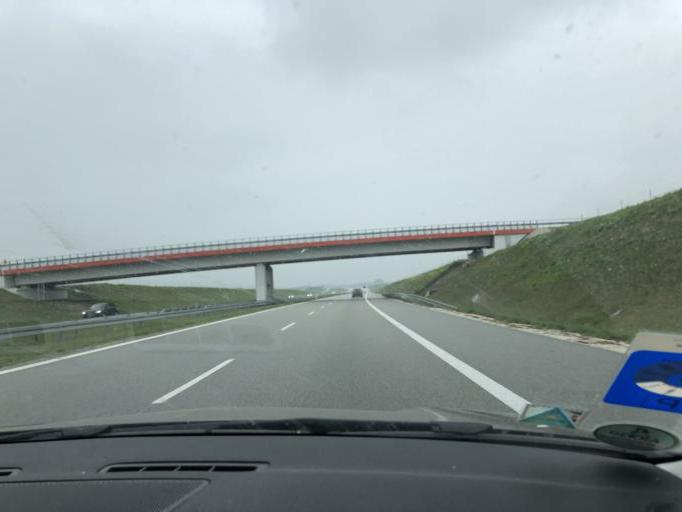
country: PL
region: Subcarpathian Voivodeship
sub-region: Powiat debicki
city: Czarna
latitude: 50.0910
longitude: 21.3012
